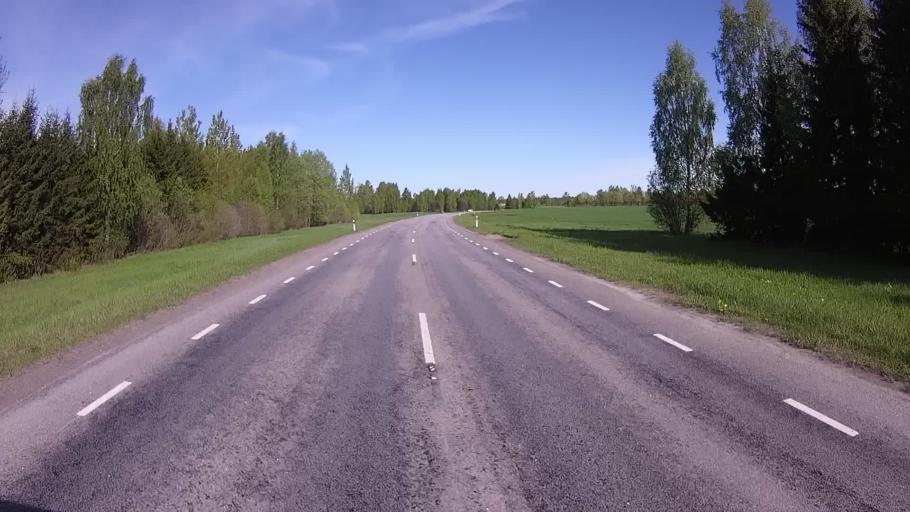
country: EE
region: Polvamaa
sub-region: Polva linn
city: Polva
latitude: 58.2450
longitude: 27.0058
